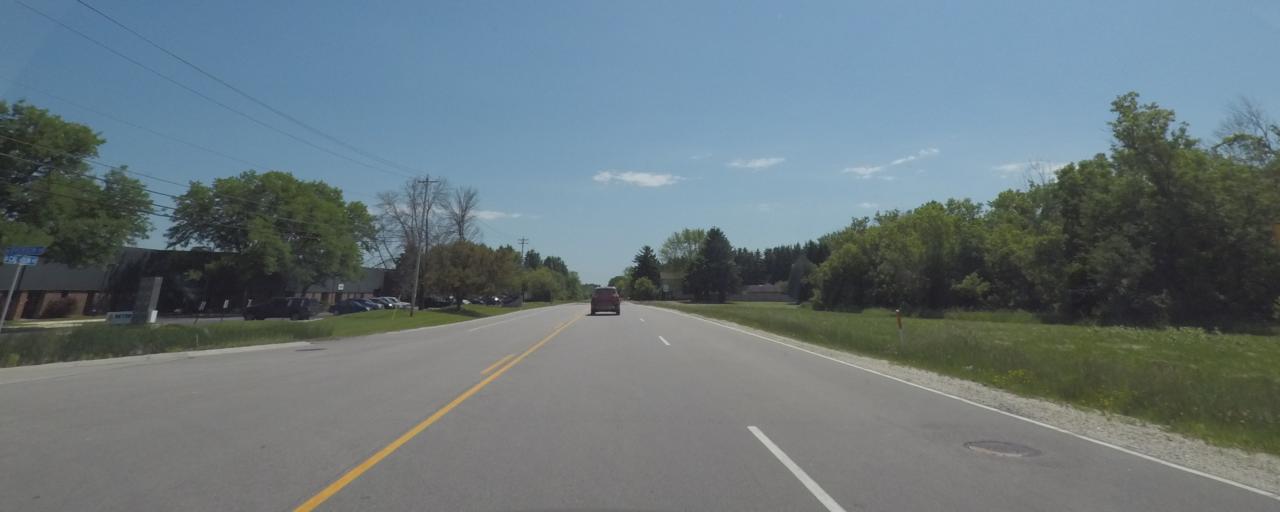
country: US
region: Wisconsin
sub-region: Waukesha County
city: New Berlin
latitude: 42.9899
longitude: -88.1281
